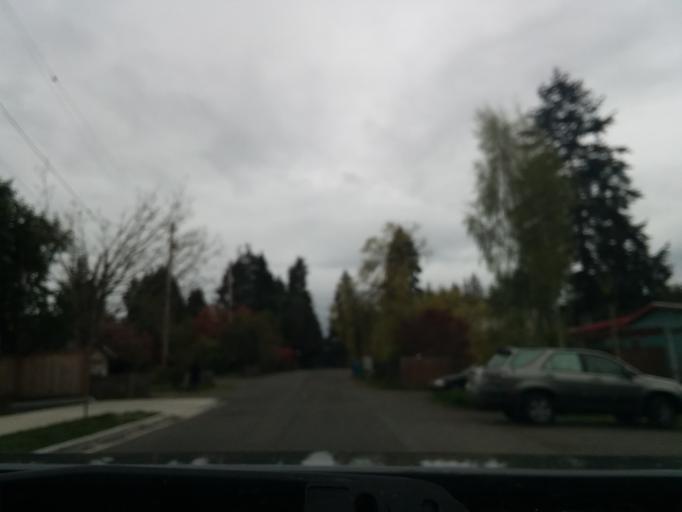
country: US
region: Washington
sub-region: King County
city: Shoreline
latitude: 47.7498
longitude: -122.3482
